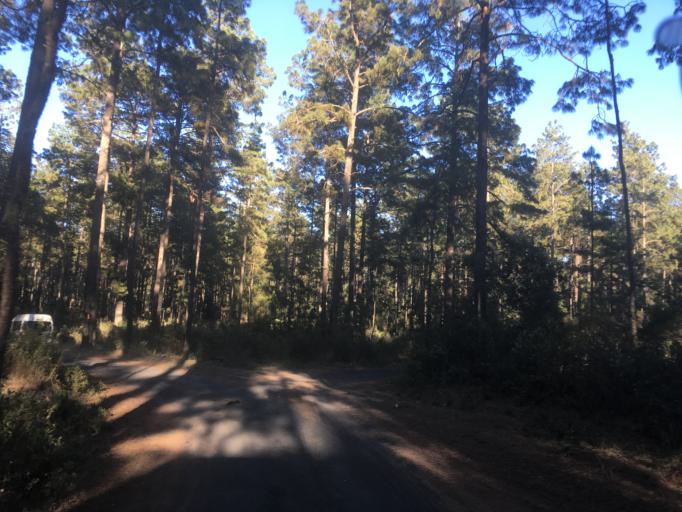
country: MX
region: Michoacan
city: Angahuan
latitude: 19.4600
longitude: -102.2116
